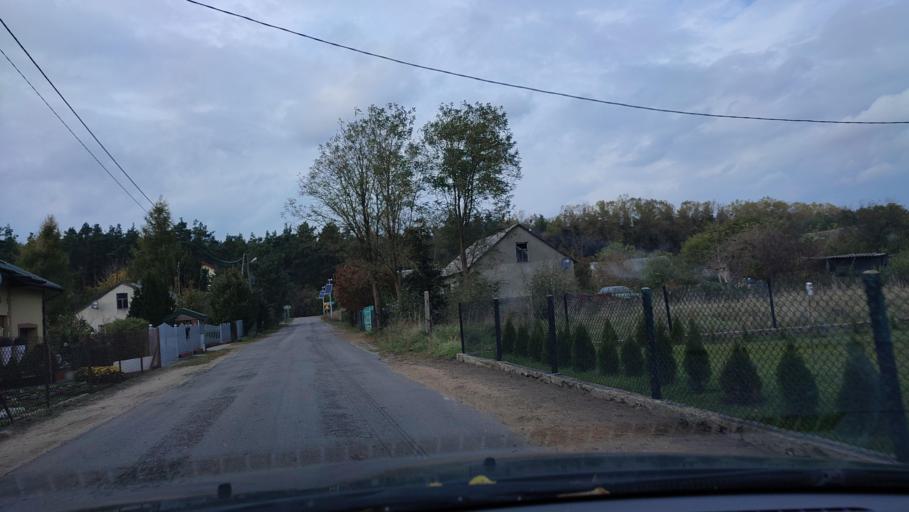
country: PL
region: Masovian Voivodeship
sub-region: Powiat mlawski
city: Mlawa
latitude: 53.1735
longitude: 20.3637
